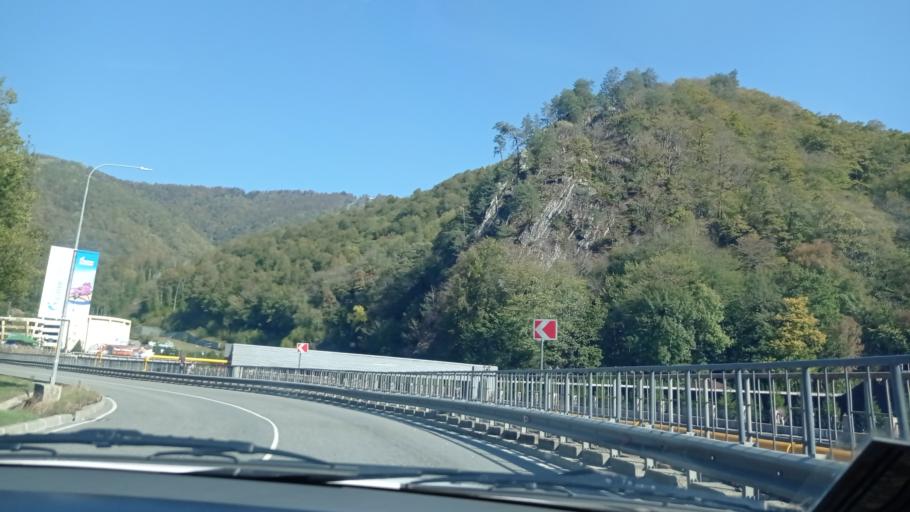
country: RU
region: Krasnodarskiy
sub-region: Sochi City
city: Krasnaya Polyana
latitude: 43.6807
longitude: 40.2764
